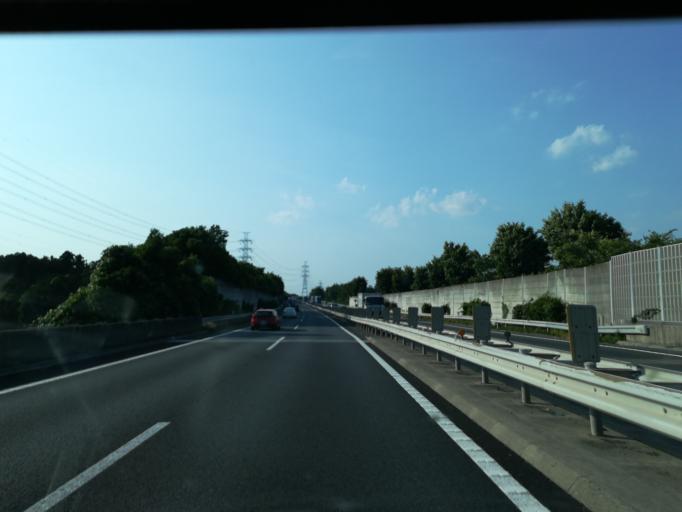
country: JP
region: Saitama
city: Sakado
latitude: 35.9065
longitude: 139.3893
